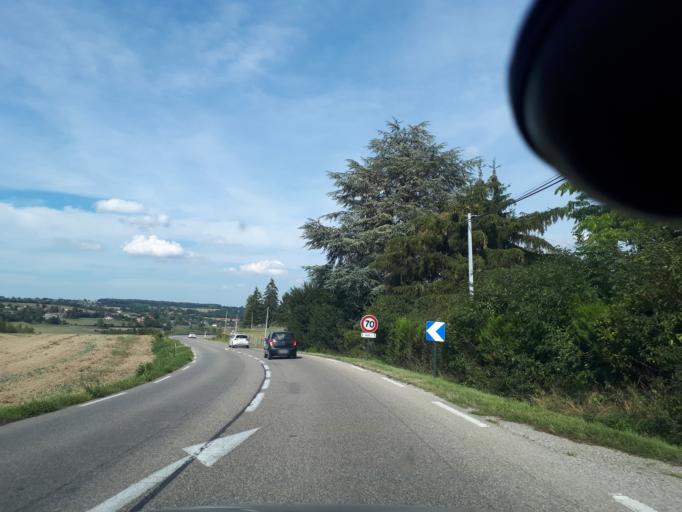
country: FR
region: Rhone-Alpes
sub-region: Departement de l'Isere
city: Maubec
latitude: 45.5364
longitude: 5.2281
